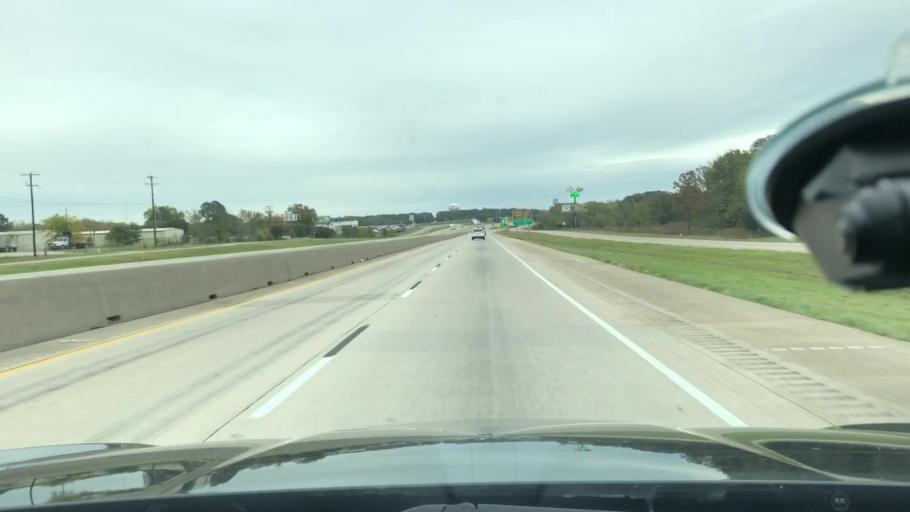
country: US
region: Texas
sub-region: Hopkins County
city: Sulphur Springs
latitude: 33.1207
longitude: -95.6460
